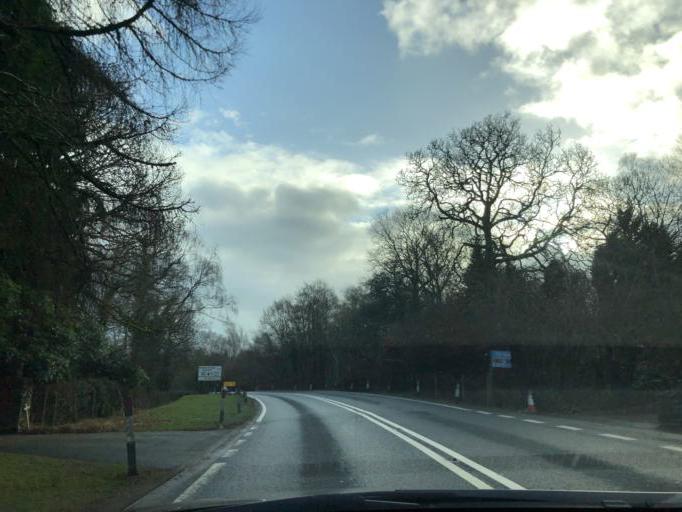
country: GB
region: England
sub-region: Cumbria
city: Grange-over-Sands
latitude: 54.2656
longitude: -2.9658
